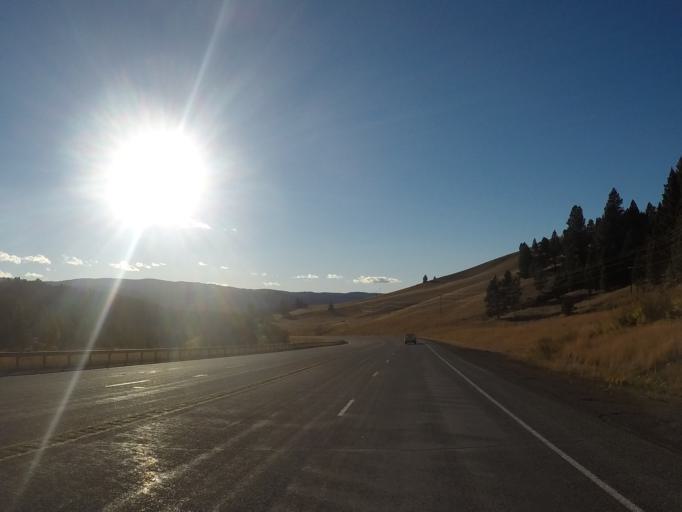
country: US
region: Montana
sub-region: Lewis and Clark County
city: Helena West Side
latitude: 46.5582
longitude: -112.3545
